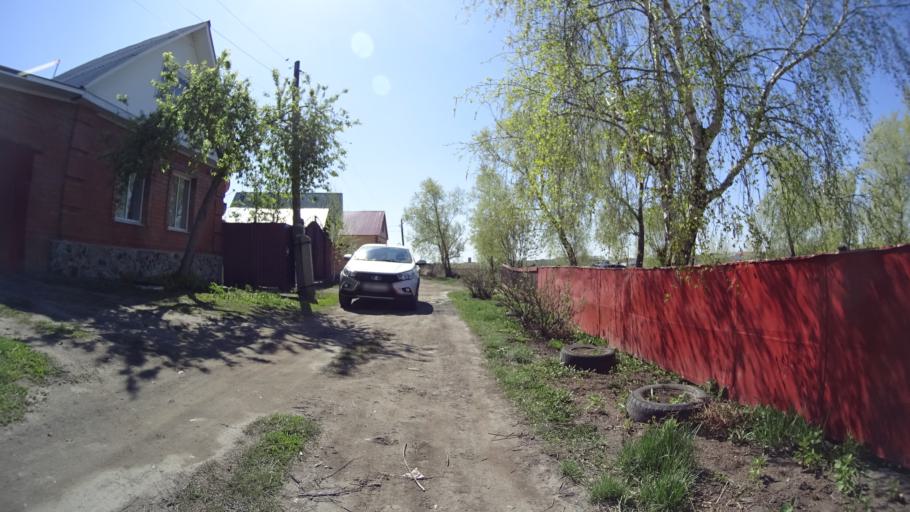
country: RU
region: Chelyabinsk
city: Troitsk
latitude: 54.0907
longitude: 61.5865
